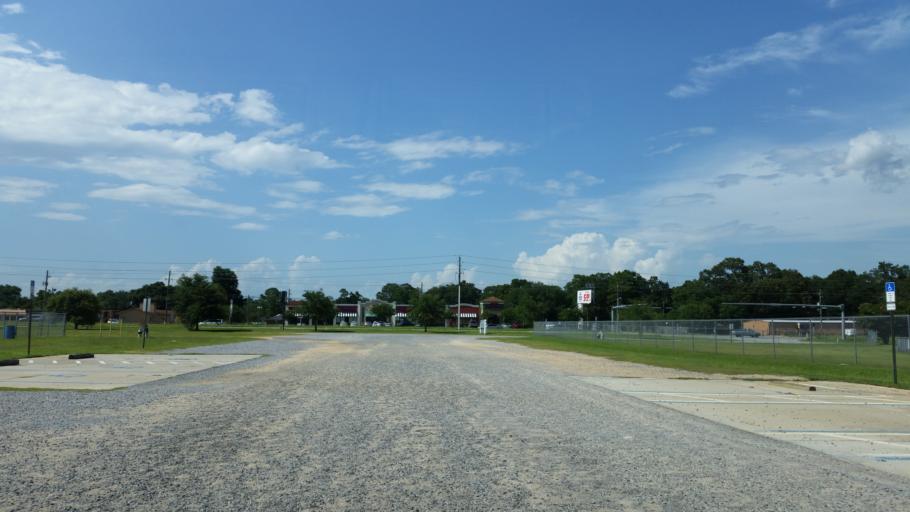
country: US
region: Florida
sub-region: Escambia County
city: Ensley
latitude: 30.5314
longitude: -87.2546
